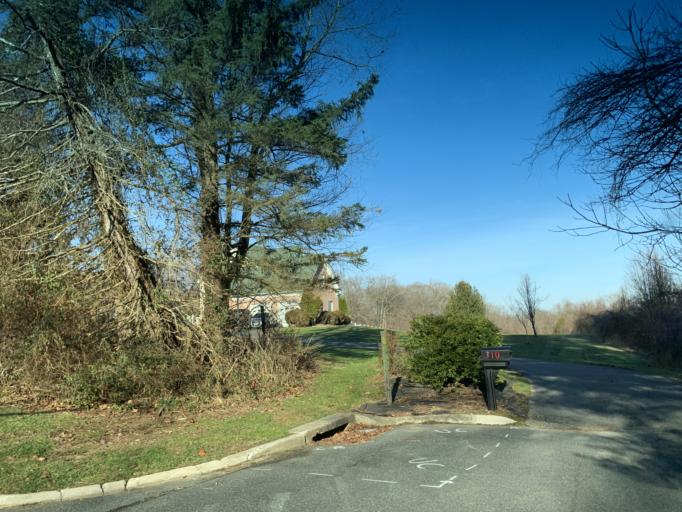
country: US
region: Maryland
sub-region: Harford County
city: South Bel Air
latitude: 39.5718
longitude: -76.2650
